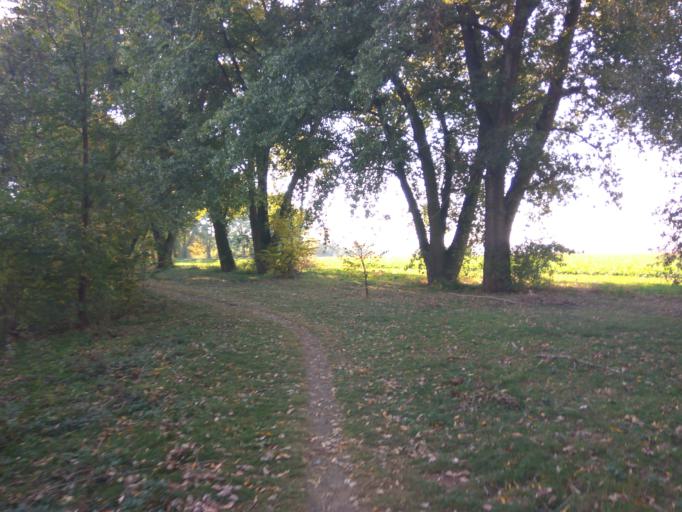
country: CZ
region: Central Bohemia
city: Hovorcovice
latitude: 50.1588
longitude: 14.5379
